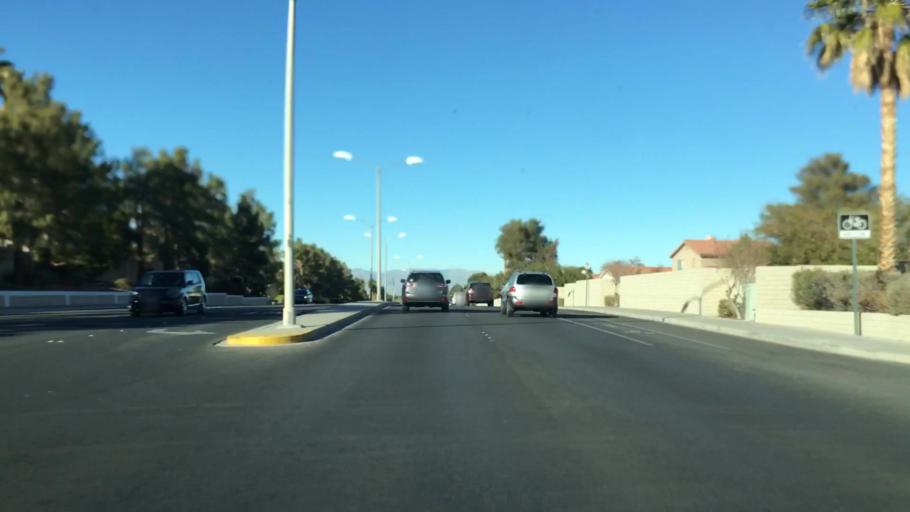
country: US
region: Nevada
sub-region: Clark County
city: Whitney
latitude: 36.0512
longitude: -115.1003
